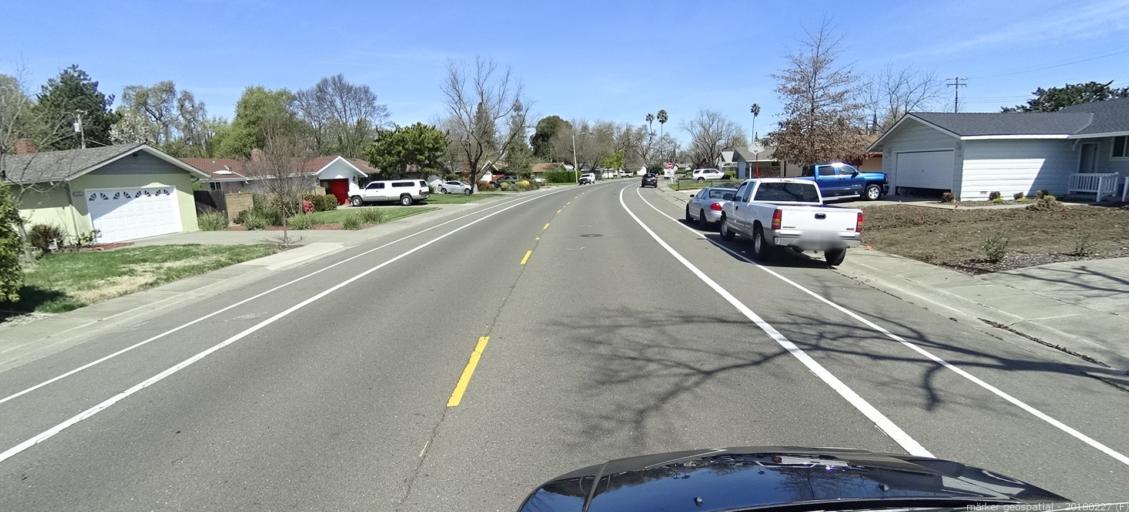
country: US
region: California
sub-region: Sacramento County
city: Rosemont
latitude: 38.5482
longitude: -121.3668
